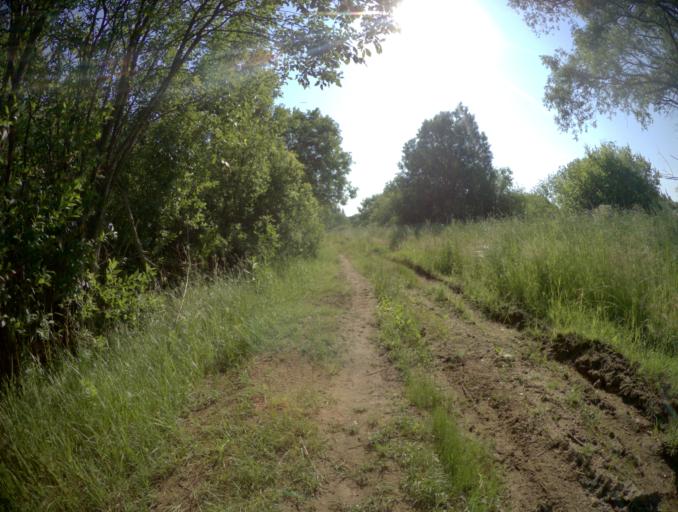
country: RU
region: Vladimir
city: Novovyazniki
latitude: 56.1965
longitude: 42.2008
